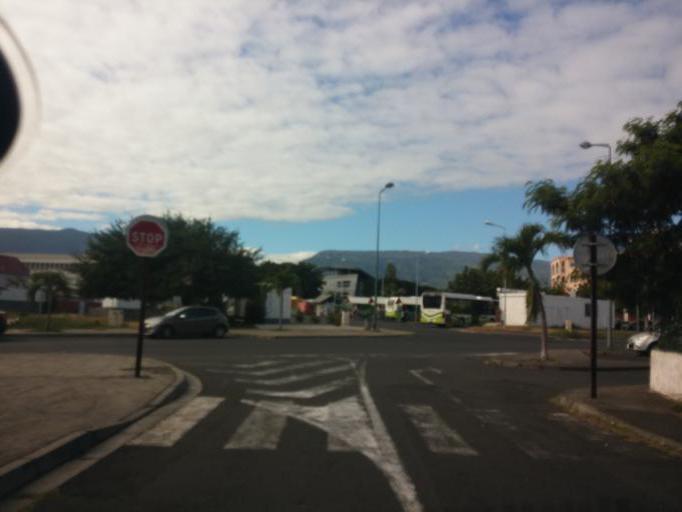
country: RE
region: Reunion
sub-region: Reunion
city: Le Port
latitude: -20.9379
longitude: 55.2965
